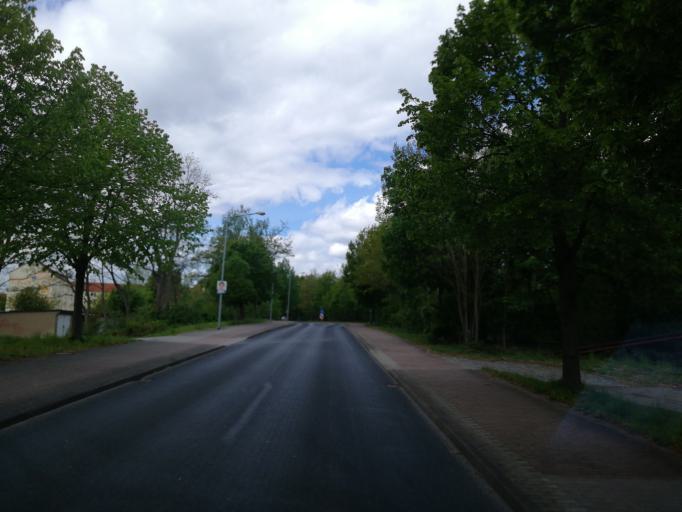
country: DE
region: Brandenburg
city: Lauchhammer
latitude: 51.4990
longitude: 13.7787
